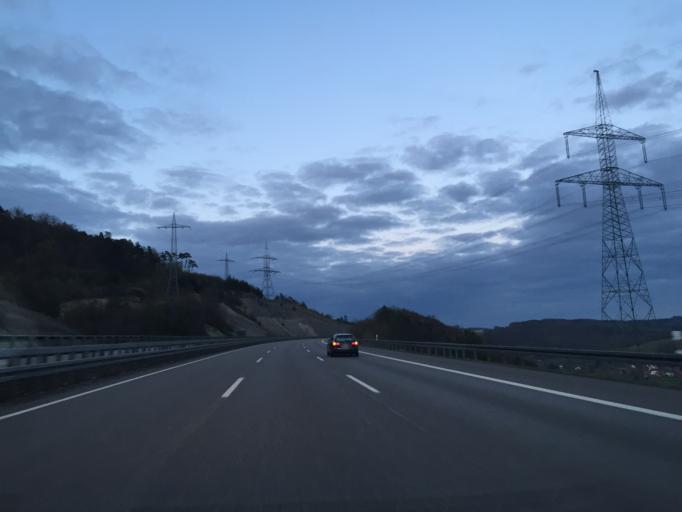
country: DE
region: Hesse
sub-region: Regierungsbezirk Kassel
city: Herleshausen
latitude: 51.0109
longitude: 10.2129
